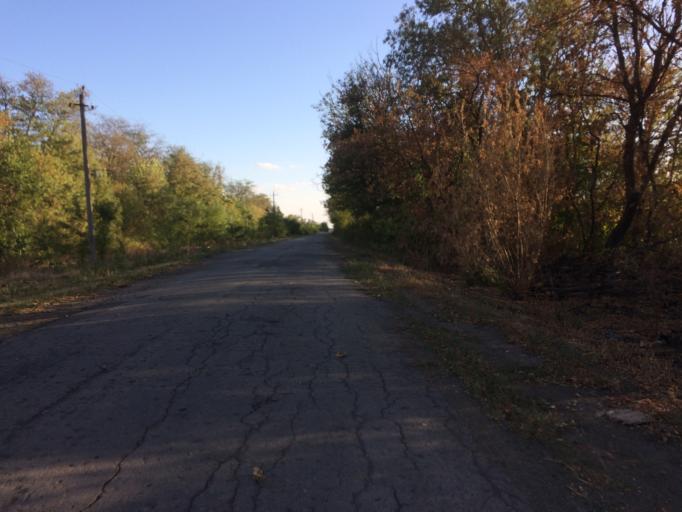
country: RU
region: Rostov
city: Gigant
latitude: 46.5121
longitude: 41.1920
